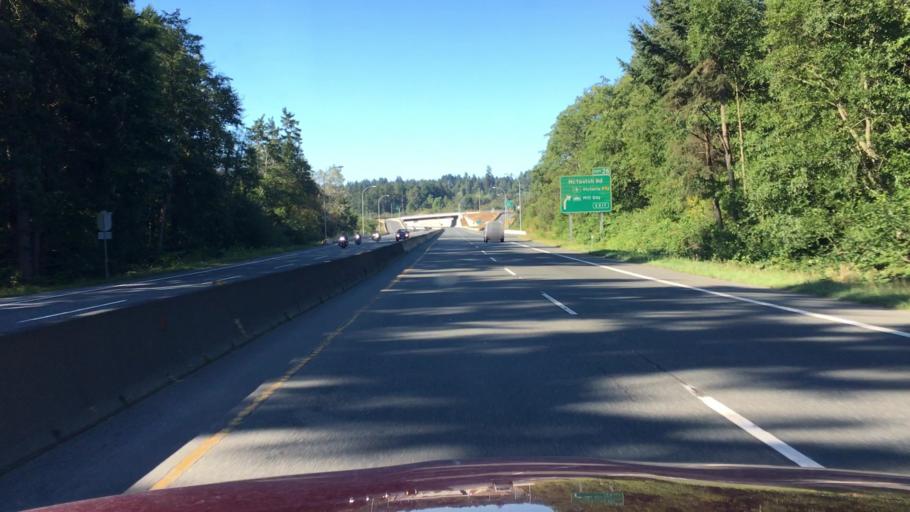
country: CA
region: British Columbia
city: North Saanich
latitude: 48.6351
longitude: -123.4100
